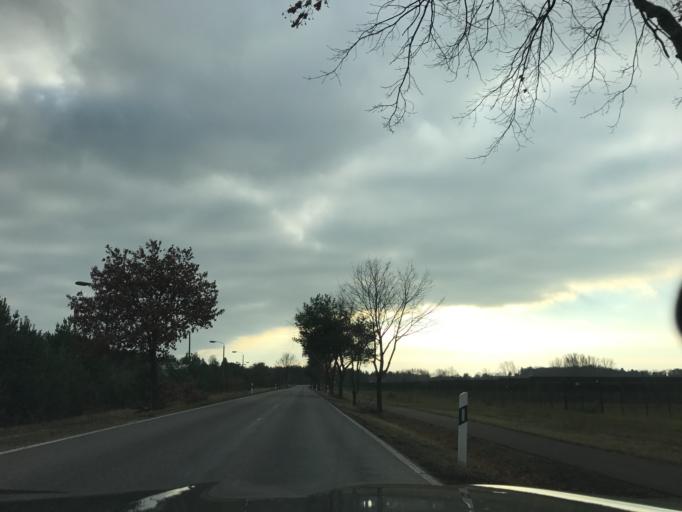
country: DE
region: Brandenburg
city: Brandenburg an der Havel
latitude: 52.3448
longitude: 12.5475
